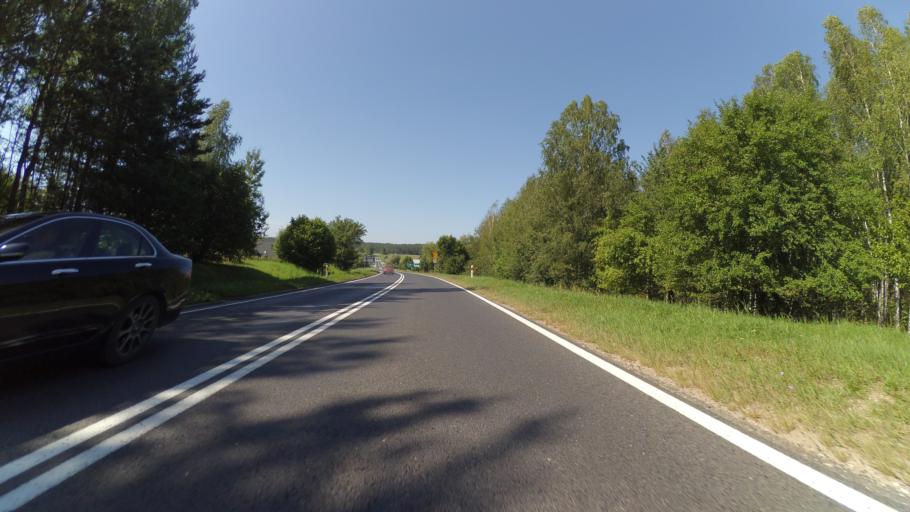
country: PL
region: Podlasie
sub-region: Powiat bialostocki
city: Suprasl
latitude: 53.1410
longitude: 23.4767
